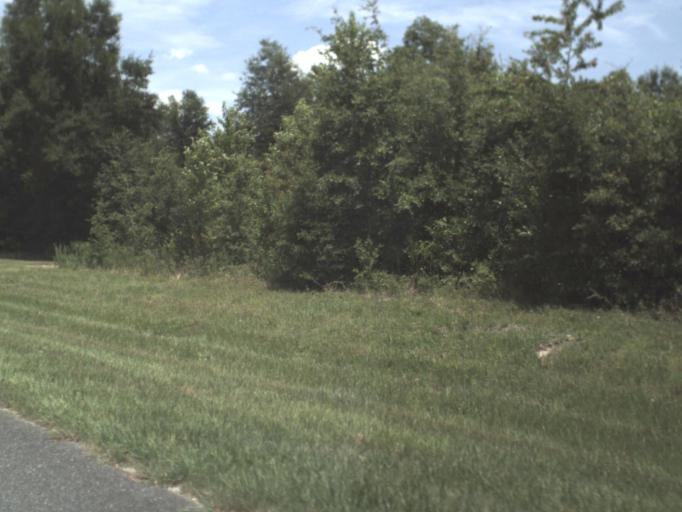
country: US
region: Florida
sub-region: Suwannee County
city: Live Oak
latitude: 30.2050
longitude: -83.0988
